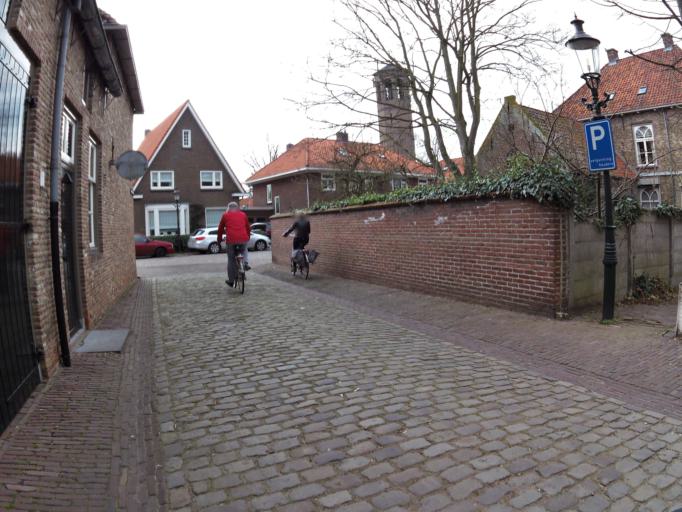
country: NL
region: North Brabant
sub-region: Gemeente Heusden
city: Heusden
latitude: 51.7335
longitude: 5.1365
